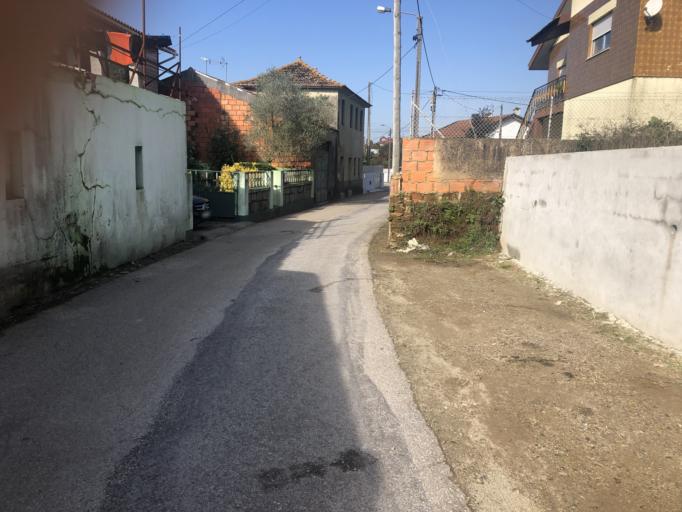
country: PT
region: Aveiro
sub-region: Estarreja
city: Beduido
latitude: 40.7674
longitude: -8.5474
